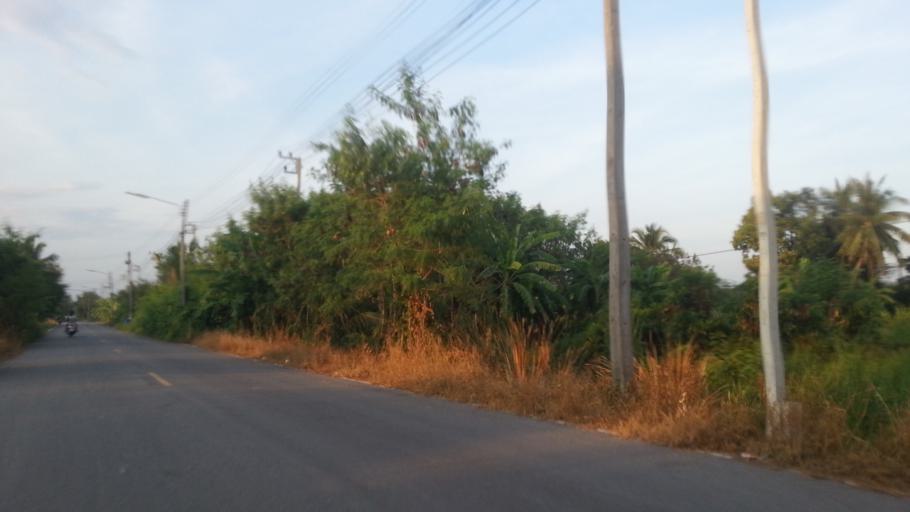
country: TH
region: Pathum Thani
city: Ban Rangsit
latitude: 14.0410
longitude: 100.8476
